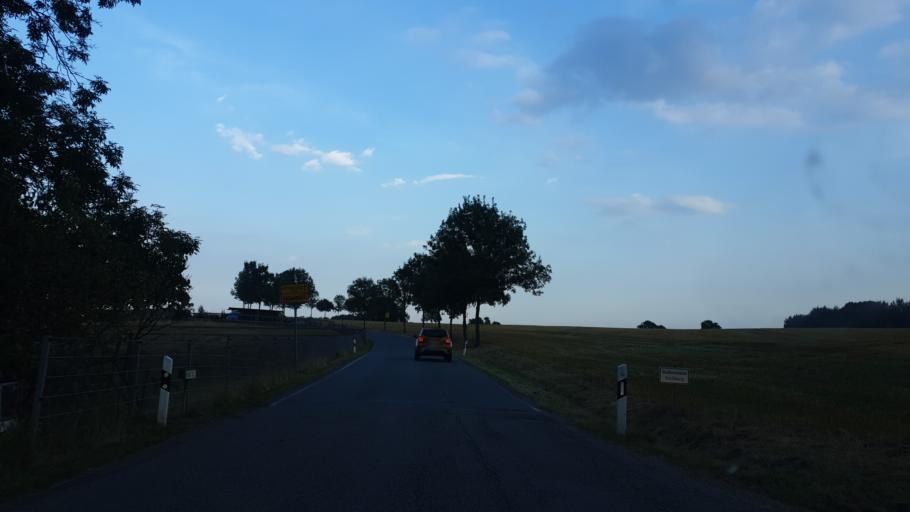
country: DE
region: Saxony
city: Kirchberg
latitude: 50.7901
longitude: 12.7889
